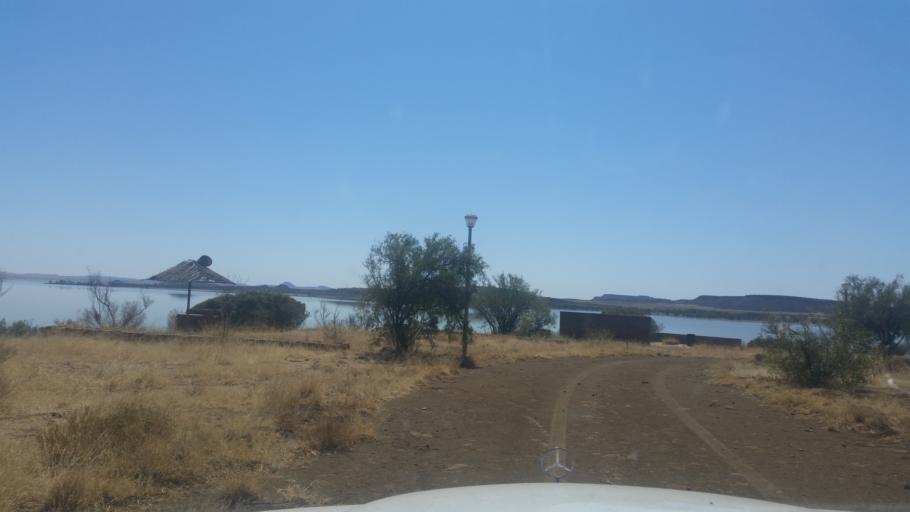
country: ZA
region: Eastern Cape
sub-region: Joe Gqabi District Municipality
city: Burgersdorp
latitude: -30.6919
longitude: 25.7763
